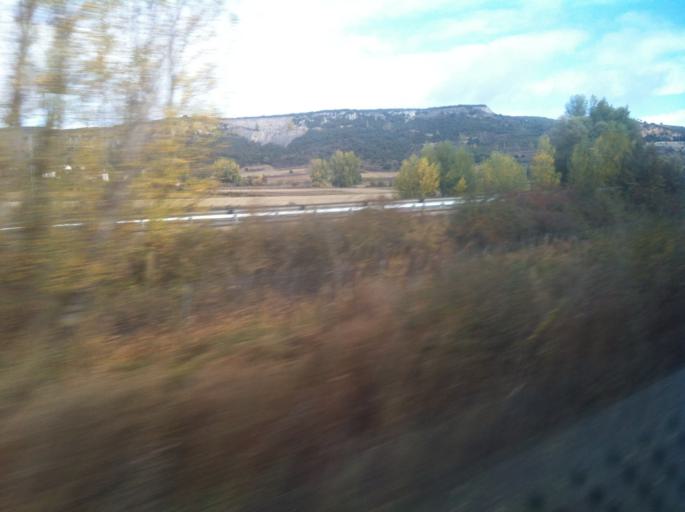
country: ES
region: Castille and Leon
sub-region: Provincia de Burgos
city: Santa Olalla de Bureba
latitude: 42.4740
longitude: -3.4381
